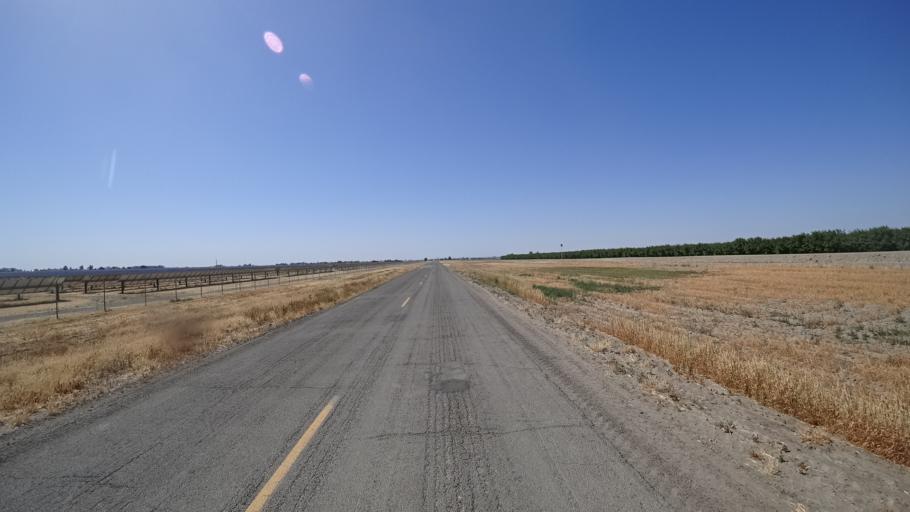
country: US
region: California
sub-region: Kings County
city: Stratford
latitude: 36.2232
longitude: -119.8340
